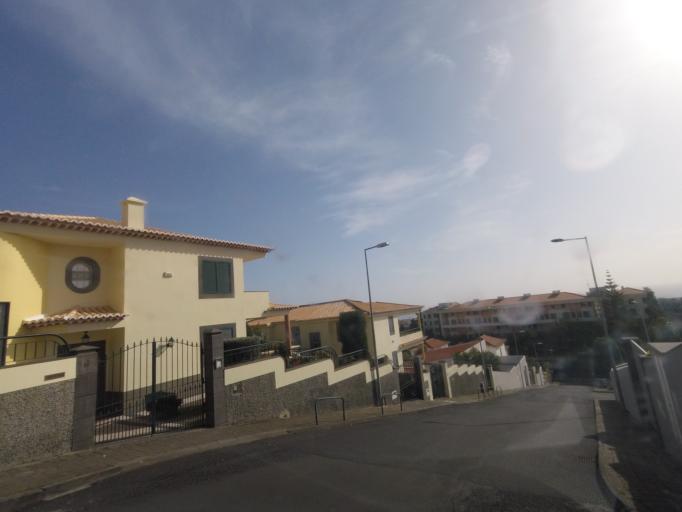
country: PT
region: Madeira
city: Camara de Lobos
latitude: 32.6396
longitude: -16.9411
